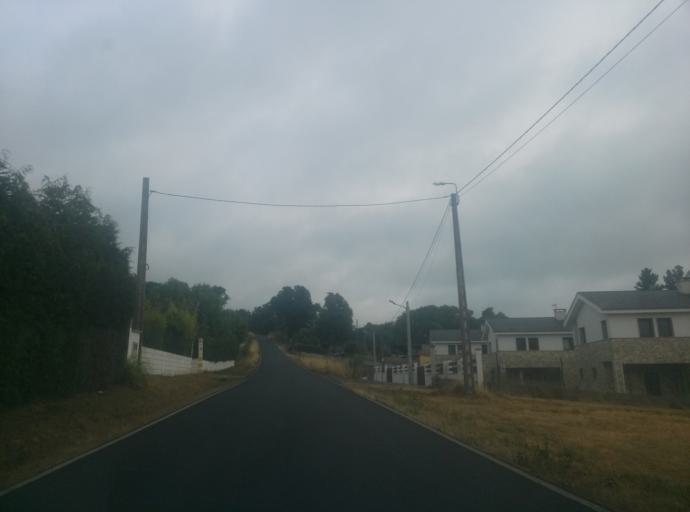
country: ES
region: Galicia
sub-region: Provincia de Lugo
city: Outeiro de Rei
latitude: 43.0833
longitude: -7.5475
